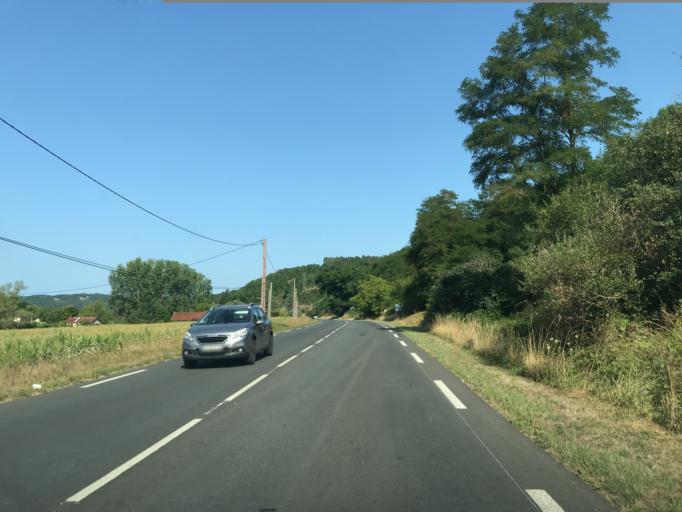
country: FR
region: Aquitaine
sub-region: Departement de la Dordogne
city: Montignac
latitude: 45.0592
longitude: 1.1976
